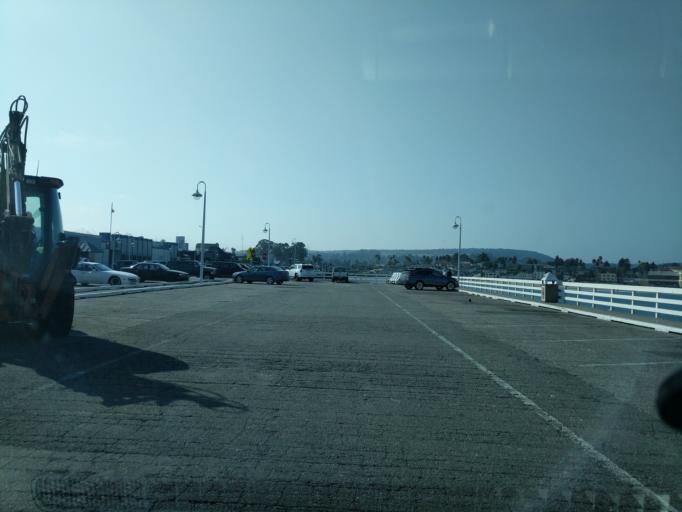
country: US
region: California
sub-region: Santa Cruz County
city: Santa Cruz
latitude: 36.9594
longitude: -122.0183
